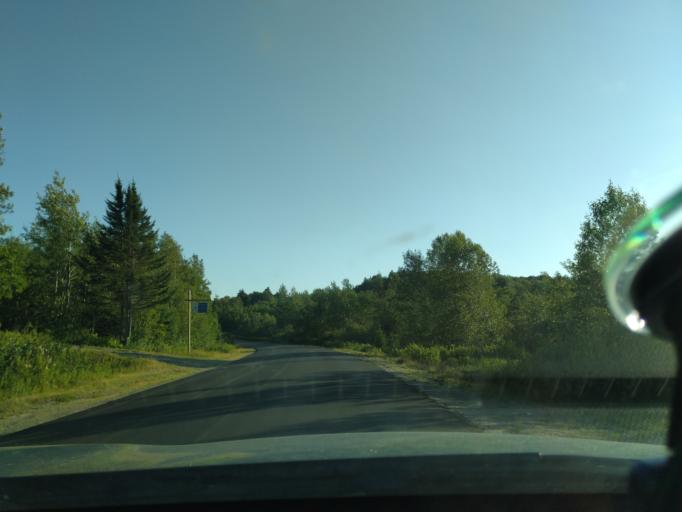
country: US
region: Maine
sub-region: Washington County
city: Eastport
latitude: 44.7173
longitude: -67.1366
